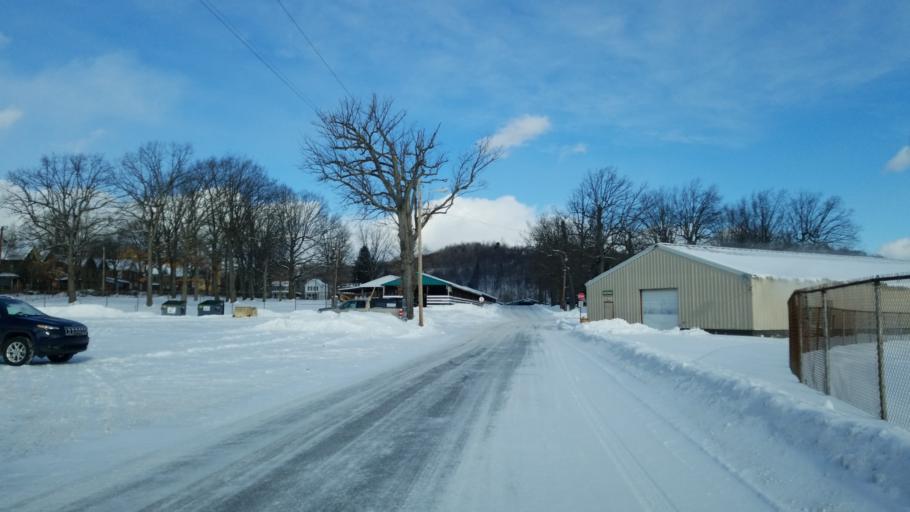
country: US
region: Pennsylvania
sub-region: Clearfield County
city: Clearfield
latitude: 41.0299
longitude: -78.4467
